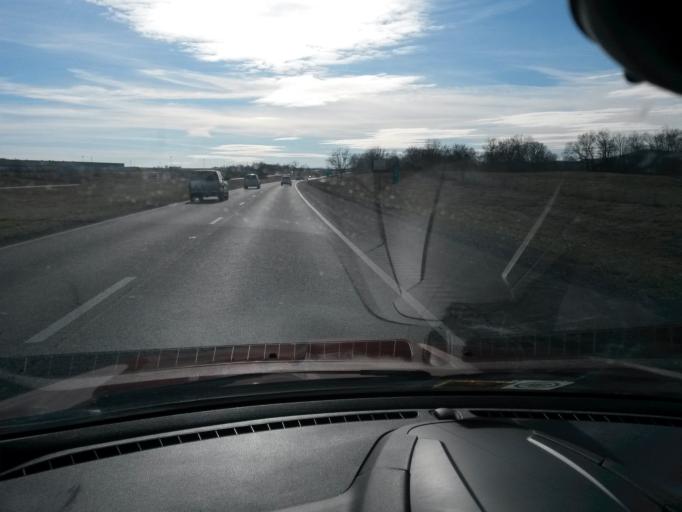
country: US
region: Virginia
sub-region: Rockingham County
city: Dayton
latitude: 38.3701
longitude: -78.9203
